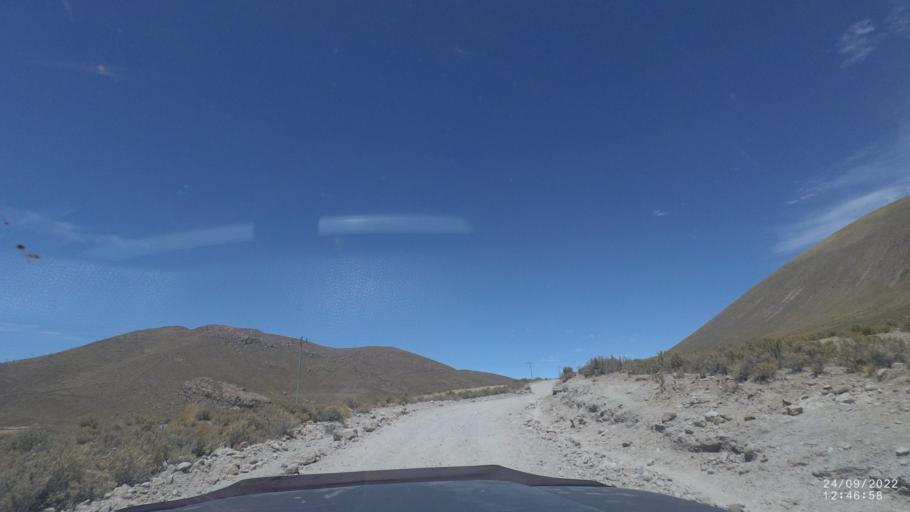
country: BO
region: Potosi
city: Colchani
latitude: -19.8064
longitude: -67.5693
